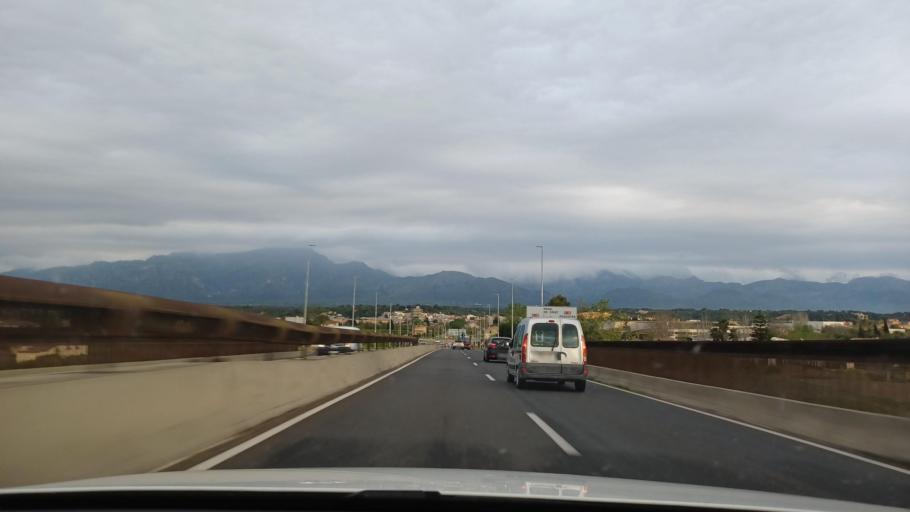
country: ES
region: Catalonia
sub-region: Provincia de Tarragona
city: Tortosa
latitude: 40.8042
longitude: 0.5105
